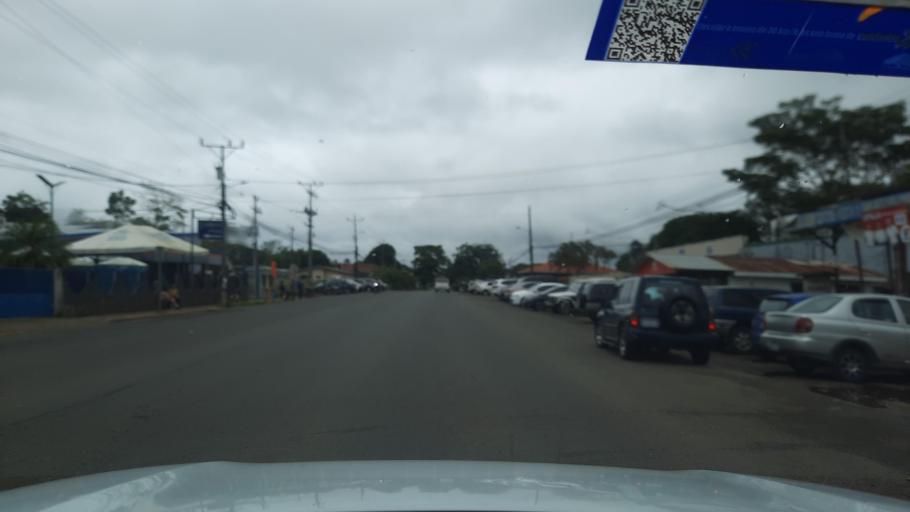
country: CR
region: Alajuela
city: Upala
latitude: 10.8978
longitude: -85.0244
